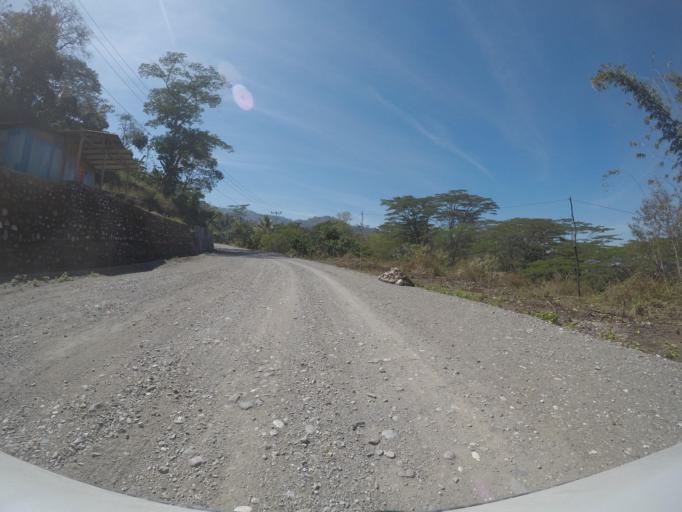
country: TL
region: Ermera
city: Gleno
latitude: -8.8076
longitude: 125.3144
